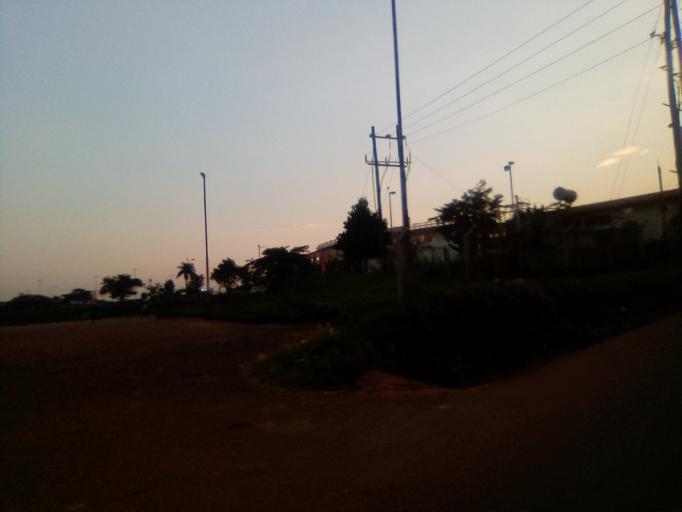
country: UG
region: Central Region
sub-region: Wakiso District
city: Kireka
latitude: 0.3459
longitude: 32.6558
